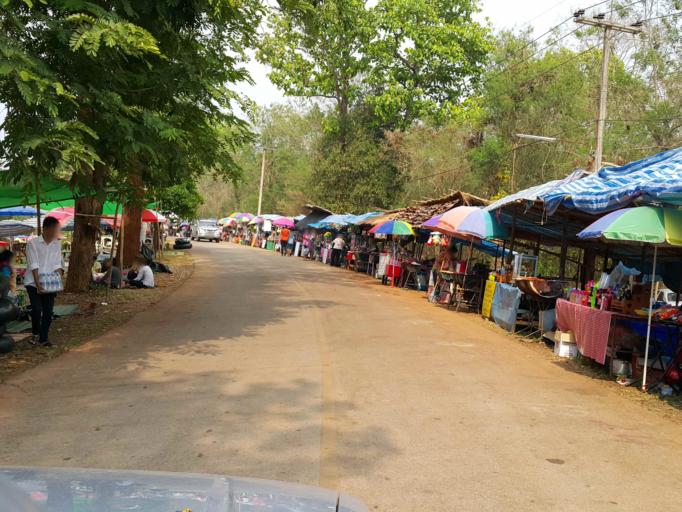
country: TH
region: Chiang Mai
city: Mae Taeng
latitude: 19.1612
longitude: 99.0317
